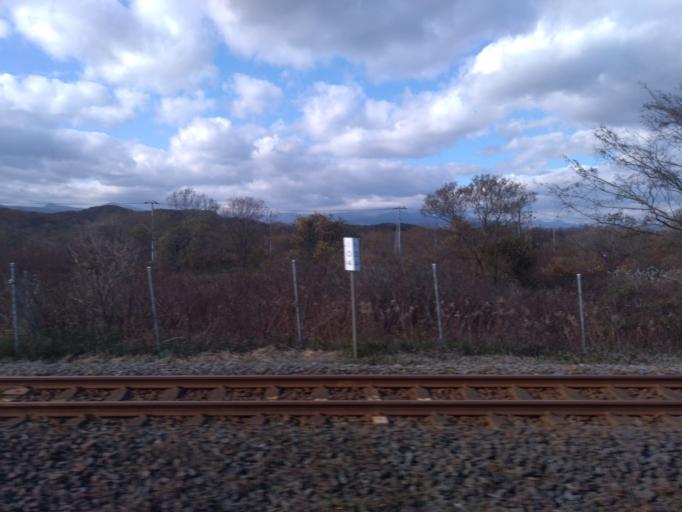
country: JP
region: Hokkaido
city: Shiraoi
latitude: 42.4992
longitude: 141.2703
